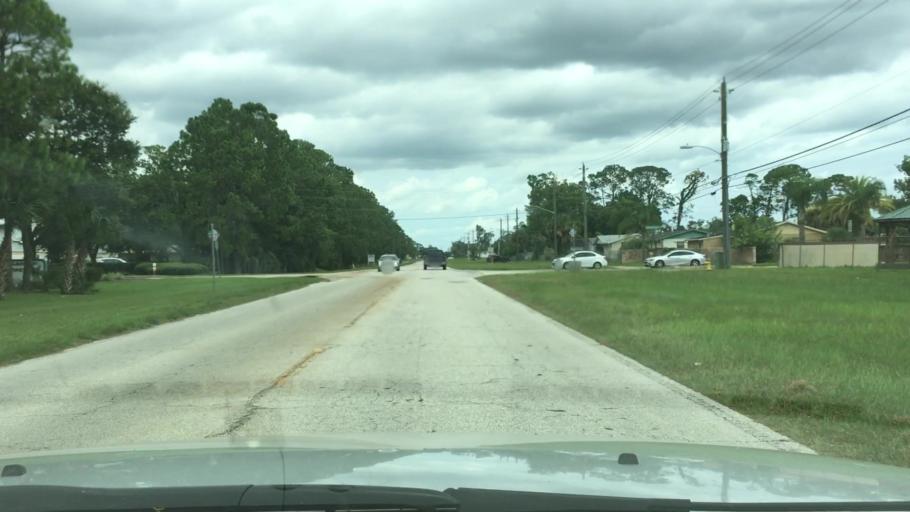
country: US
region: Florida
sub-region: Volusia County
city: Holly Hill
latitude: 29.2174
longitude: -81.0703
